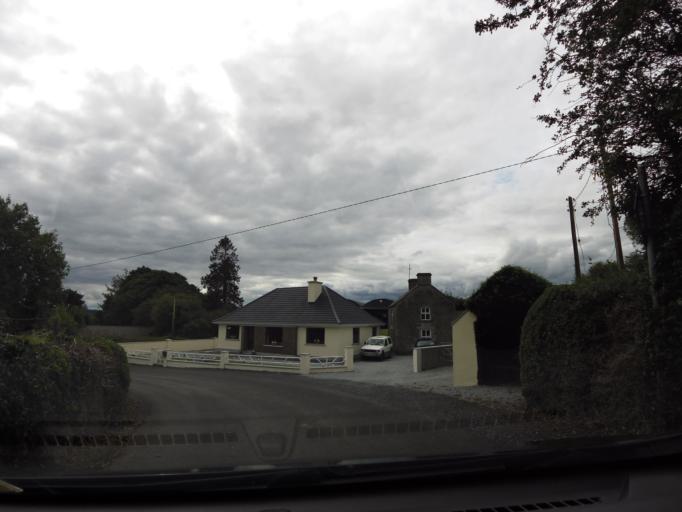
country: IE
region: Connaught
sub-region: County Galway
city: Loughrea
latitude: 53.1572
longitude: -8.4336
